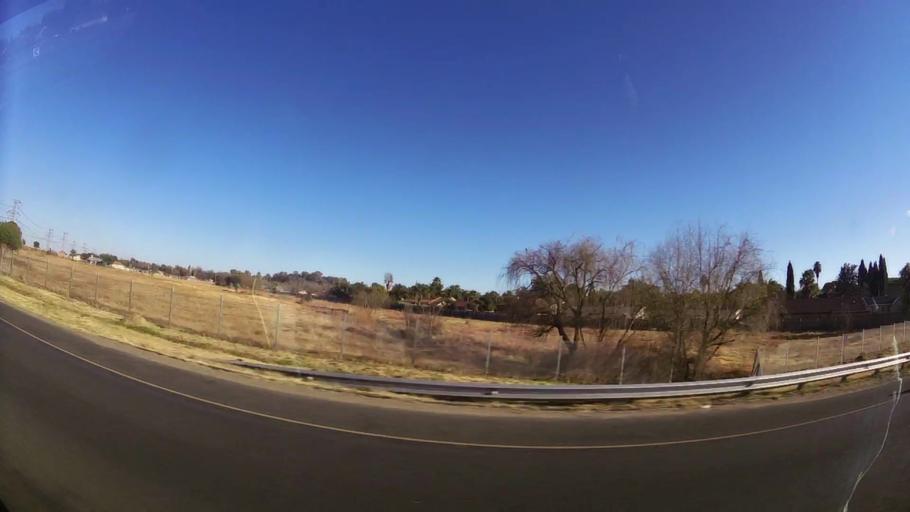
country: ZA
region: Gauteng
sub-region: City of Johannesburg Metropolitan Municipality
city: Modderfontein
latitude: -26.0860
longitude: 28.2039
